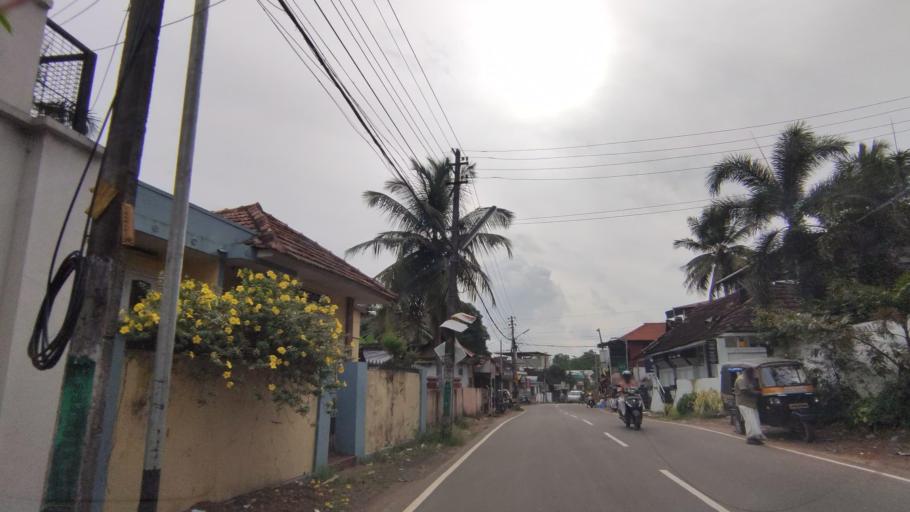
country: IN
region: Kerala
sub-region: Kottayam
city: Kottayam
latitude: 9.5834
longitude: 76.5087
